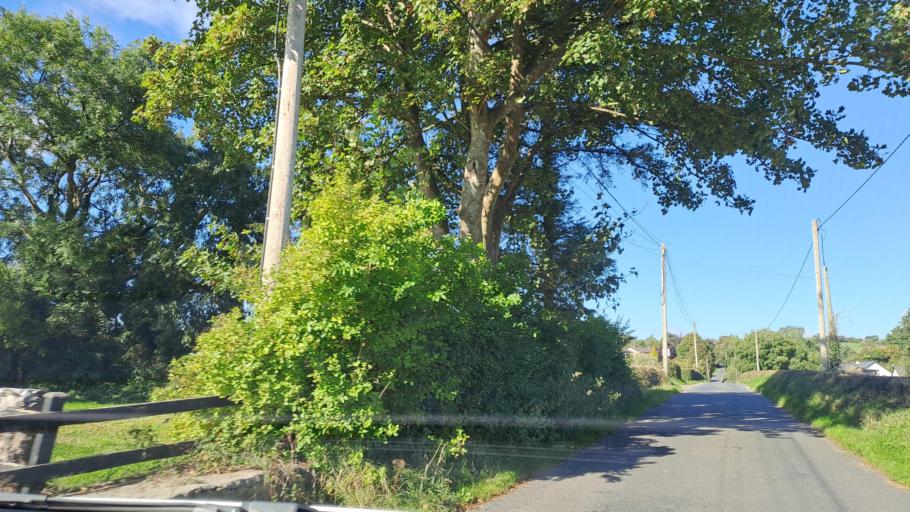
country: IE
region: Ulster
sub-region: County Monaghan
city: Carrickmacross
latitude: 53.9880
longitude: -6.7491
